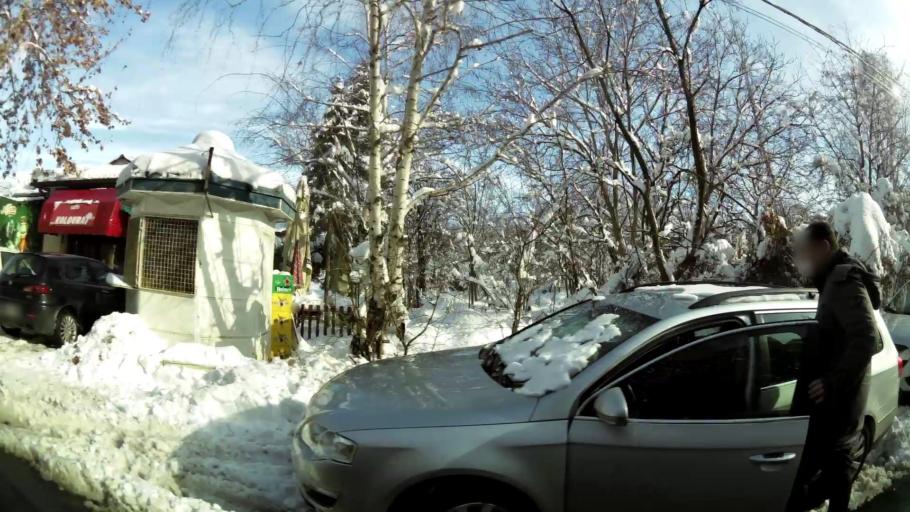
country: RS
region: Central Serbia
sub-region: Belgrade
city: Zvezdara
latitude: 44.7883
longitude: 20.5463
